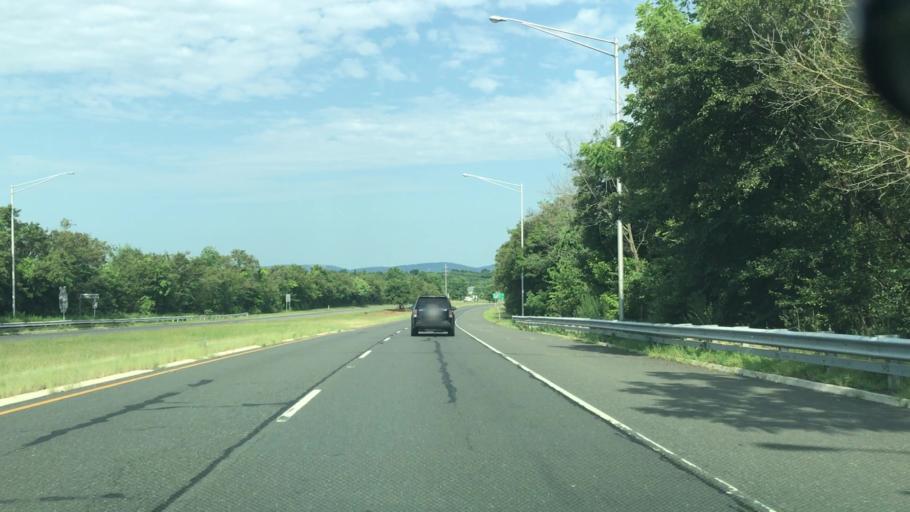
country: US
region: New Jersey
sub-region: Somerset County
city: Bridgewater
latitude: 40.5943
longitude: -74.6641
